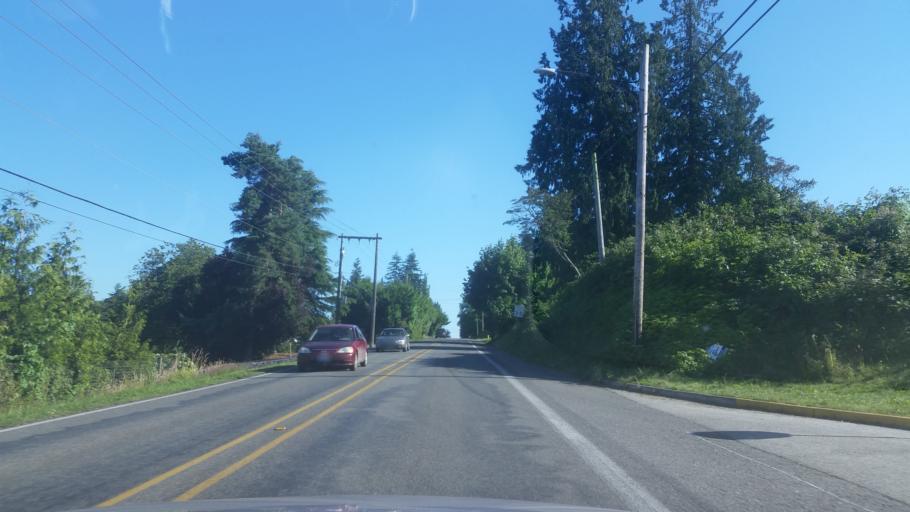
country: US
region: Washington
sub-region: Snohomish County
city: Cathcart
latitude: 47.8666
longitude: -122.0991
